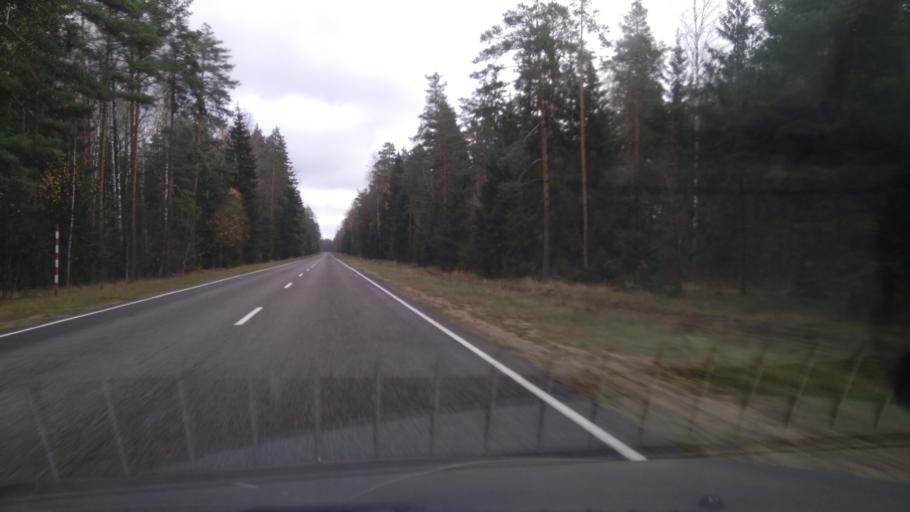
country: BY
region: Minsk
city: Urechcha
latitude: 53.2117
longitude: 27.8197
